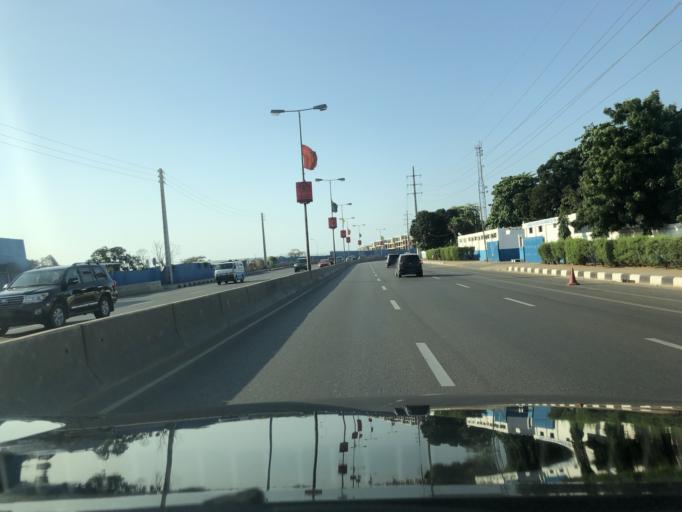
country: AO
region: Luanda
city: Luanda
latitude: -8.9007
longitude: 13.1768
